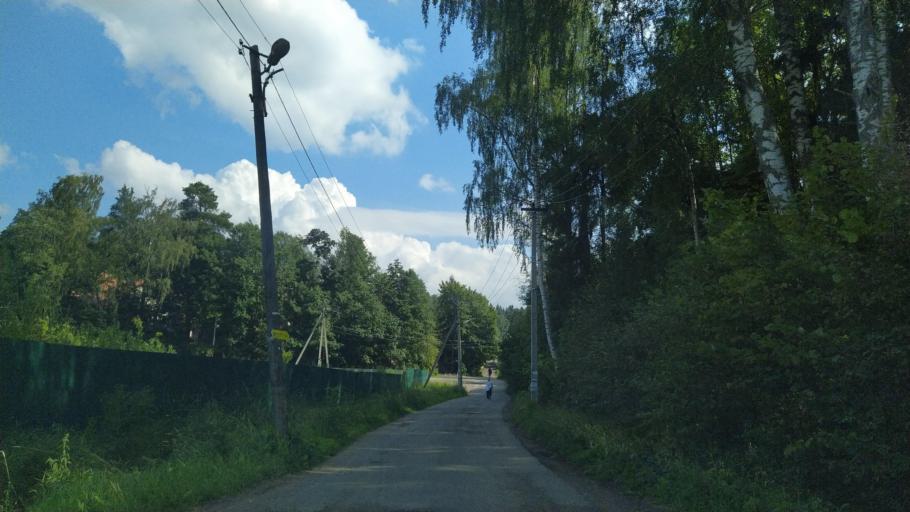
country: RU
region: Leningrad
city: Toksovo
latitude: 60.1737
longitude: 30.5280
